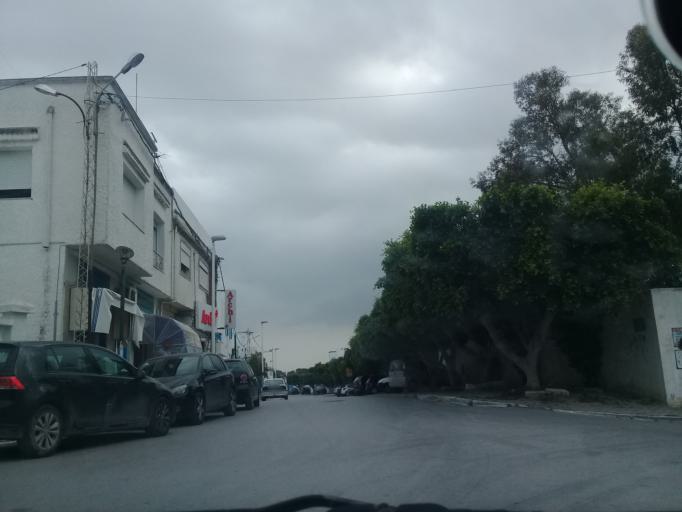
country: TN
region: Tunis
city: Sidi Bou Said
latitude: 36.8711
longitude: 10.3372
